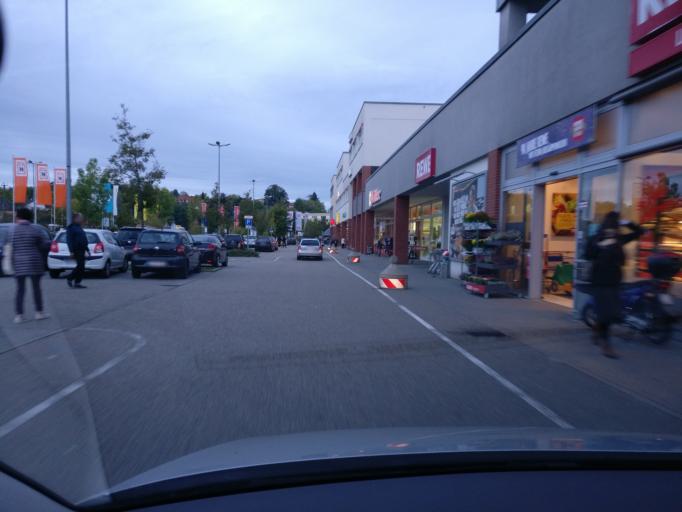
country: DE
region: Baden-Wuerttemberg
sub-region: Karlsruhe Region
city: Bretten
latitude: 49.0320
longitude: 8.7044
